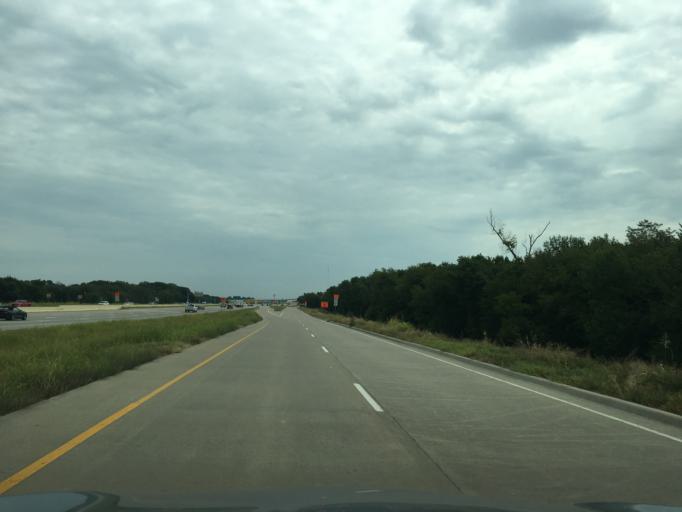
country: US
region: Texas
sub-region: Collin County
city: Melissa
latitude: 33.2529
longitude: -96.6143
